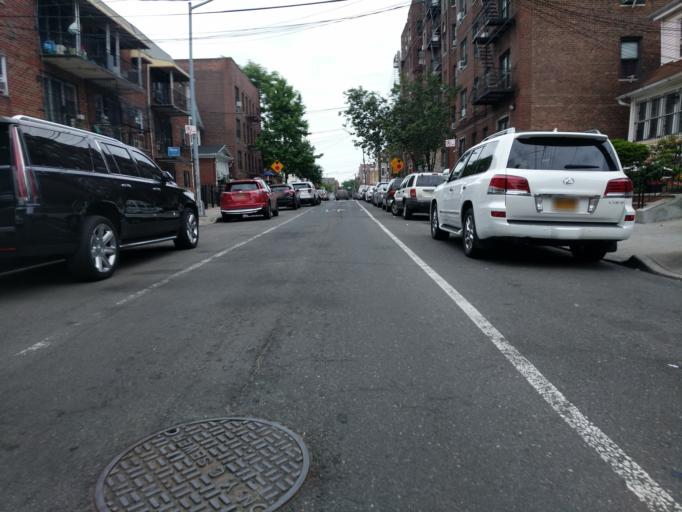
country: US
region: New York
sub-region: Queens County
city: Long Island City
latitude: 40.7457
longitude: -73.8818
